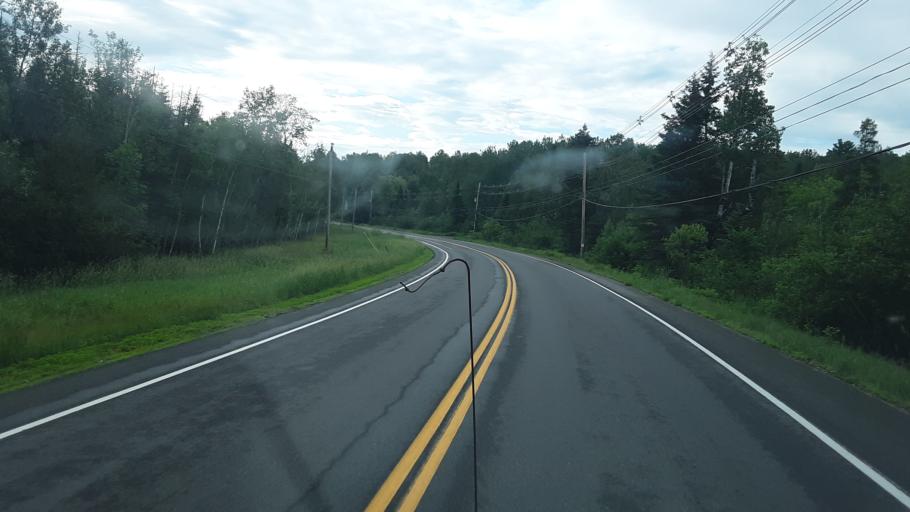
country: US
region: Maine
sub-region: Penobscot County
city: Patten
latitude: 45.8883
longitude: -68.4232
